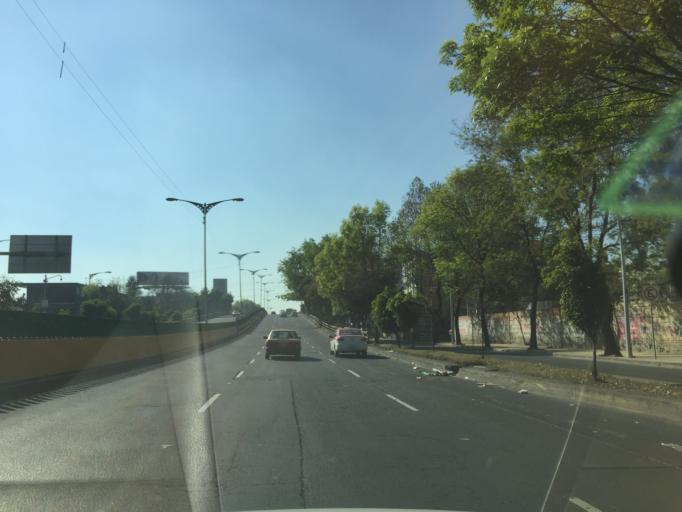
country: MX
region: Mexico City
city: Azcapotzalco
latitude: 19.4722
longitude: -99.1895
